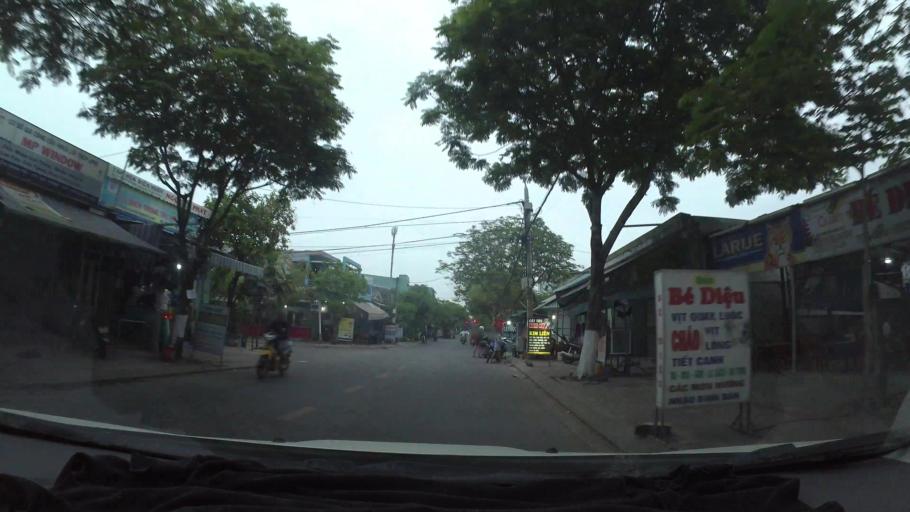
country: VN
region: Da Nang
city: Thanh Khe
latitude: 16.0499
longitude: 108.1767
